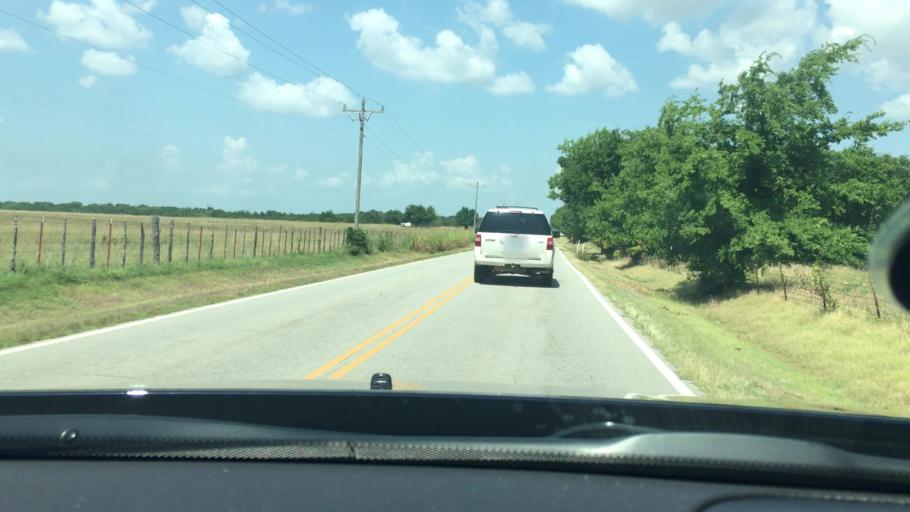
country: US
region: Oklahoma
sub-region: Bryan County
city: Durant
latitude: 34.0848
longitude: -96.4178
